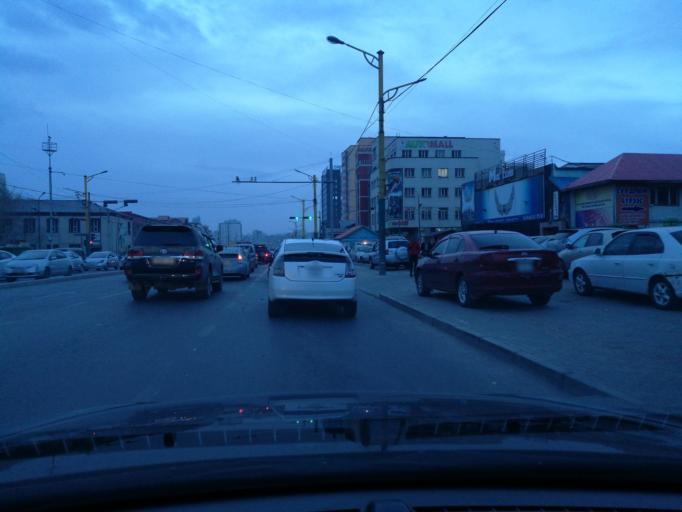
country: MN
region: Ulaanbaatar
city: Ulaanbaatar
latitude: 47.9290
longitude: 106.9153
